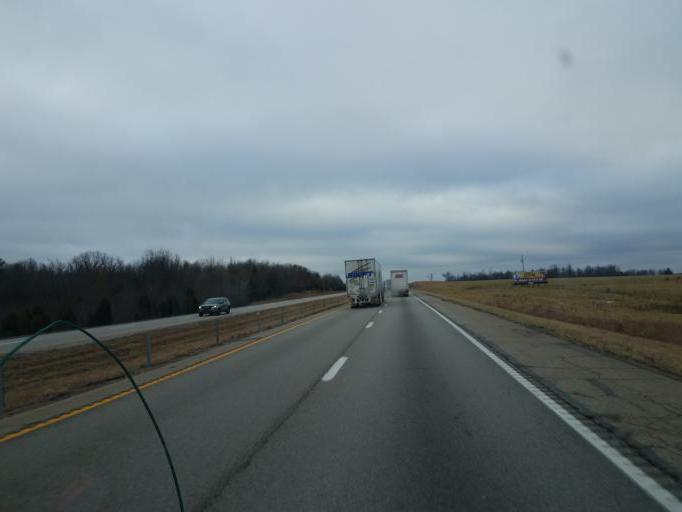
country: US
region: Missouri
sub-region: Laclede County
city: Lebanon
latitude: 37.5424
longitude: -92.8144
